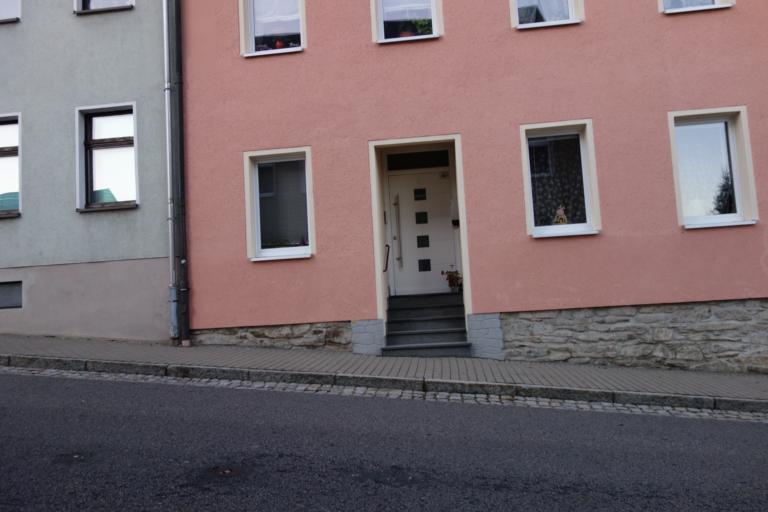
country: DE
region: Saxony
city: Johstadt
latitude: 50.5132
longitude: 13.0919
